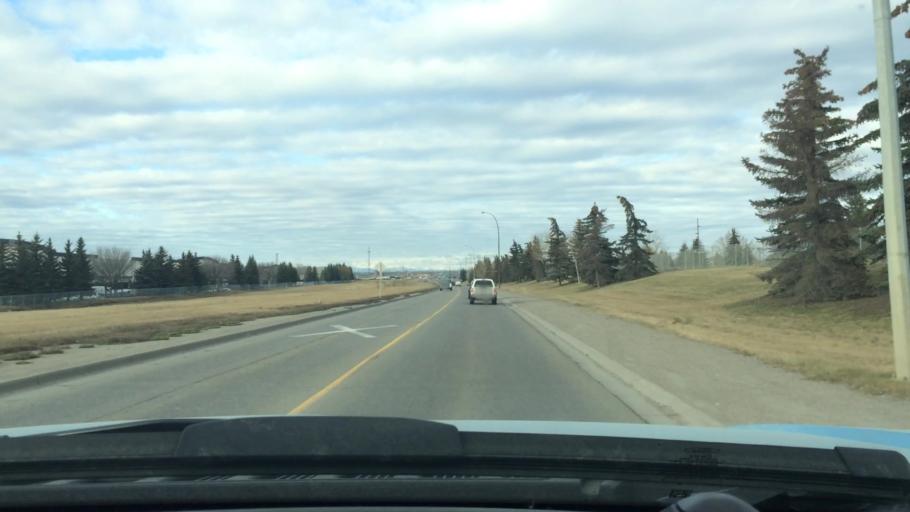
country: CA
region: Alberta
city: Calgary
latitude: 51.0154
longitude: -113.9869
